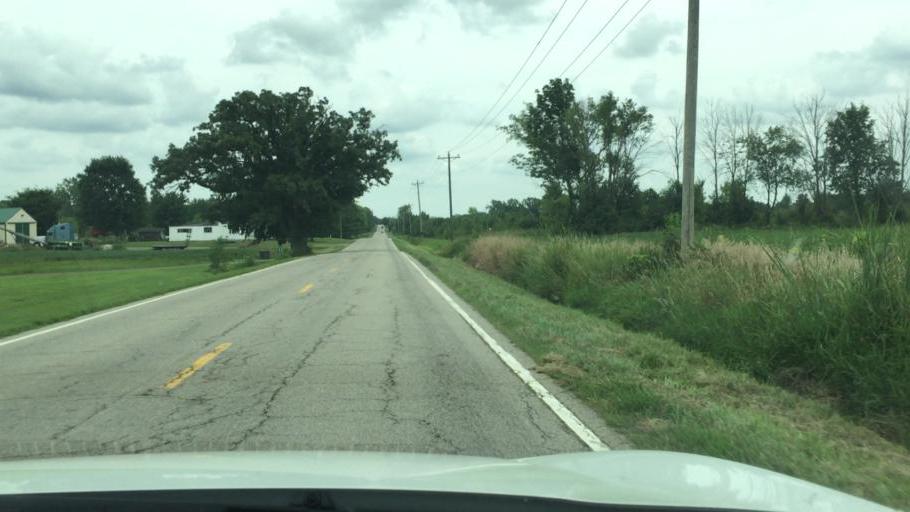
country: US
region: Ohio
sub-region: Champaign County
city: North Lewisburg
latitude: 40.2529
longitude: -83.4866
